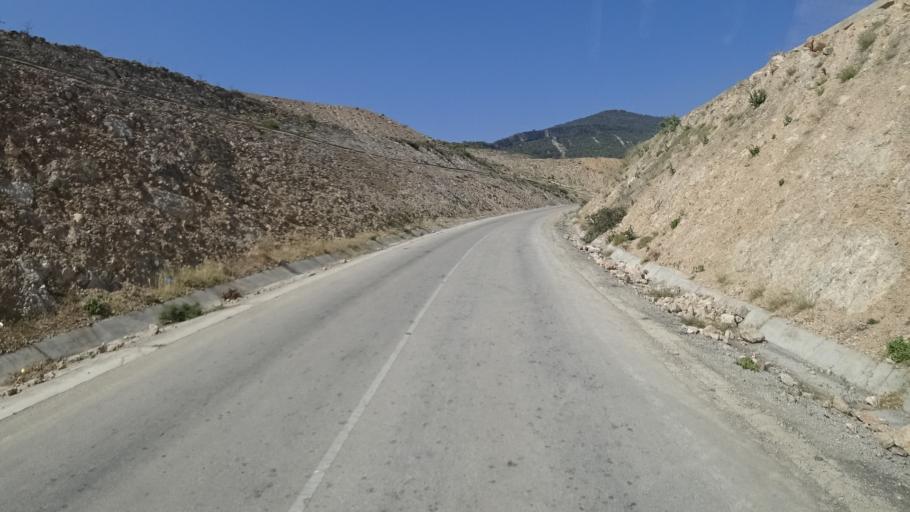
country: OM
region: Zufar
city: Salalah
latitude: 17.0444
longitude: 54.6128
